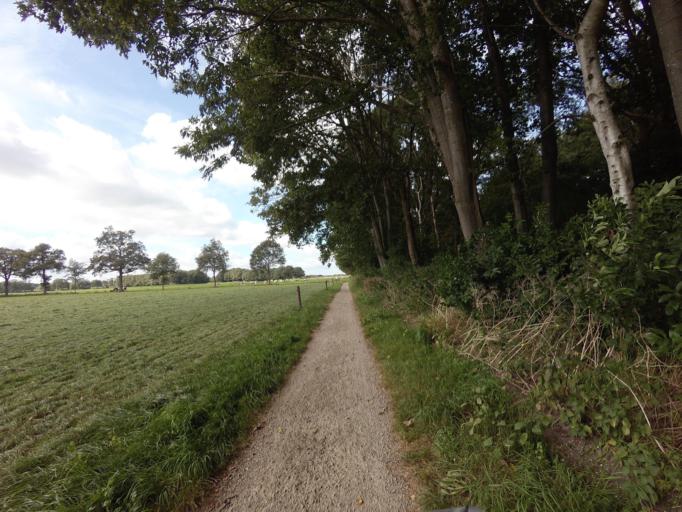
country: NL
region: Overijssel
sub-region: Gemeente Deventer
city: Schalkhaar
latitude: 52.2953
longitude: 6.2490
